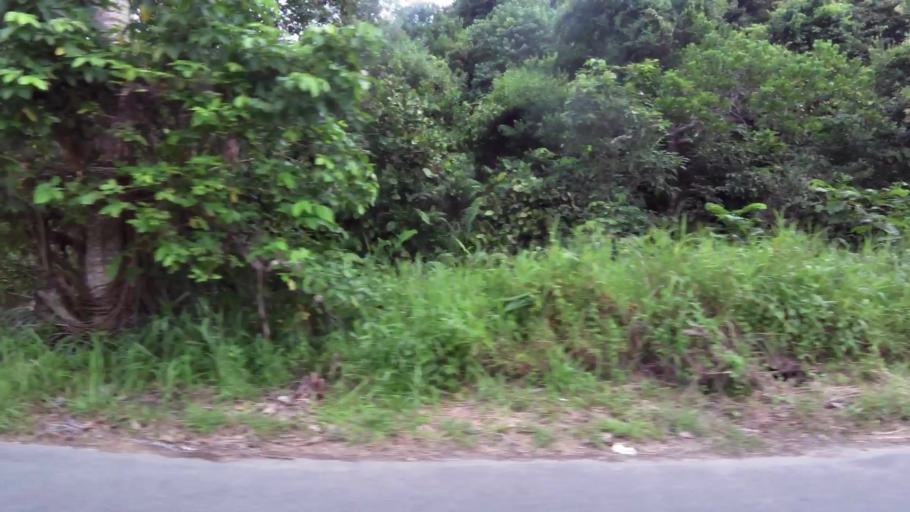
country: BN
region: Brunei and Muara
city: Bandar Seri Begawan
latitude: 4.9615
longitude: 114.9872
